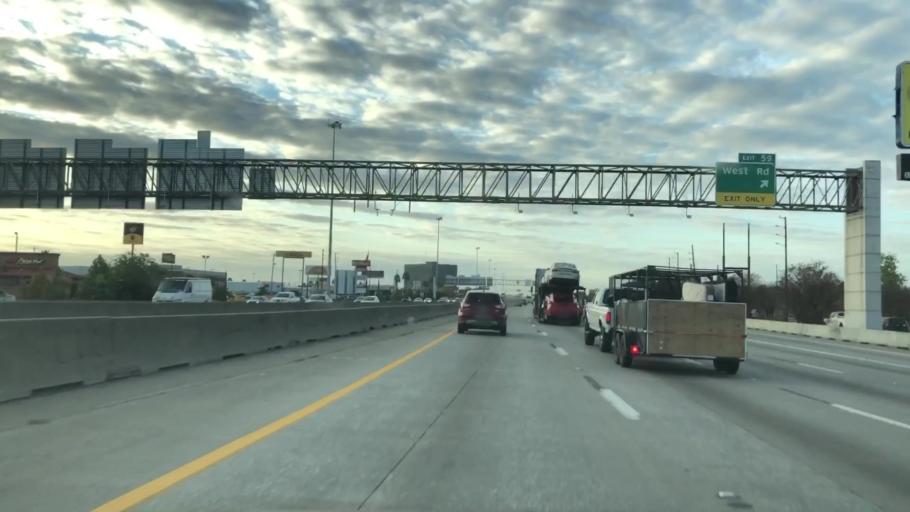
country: US
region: Texas
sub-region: Harris County
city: Aldine
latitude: 29.9298
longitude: -95.4120
